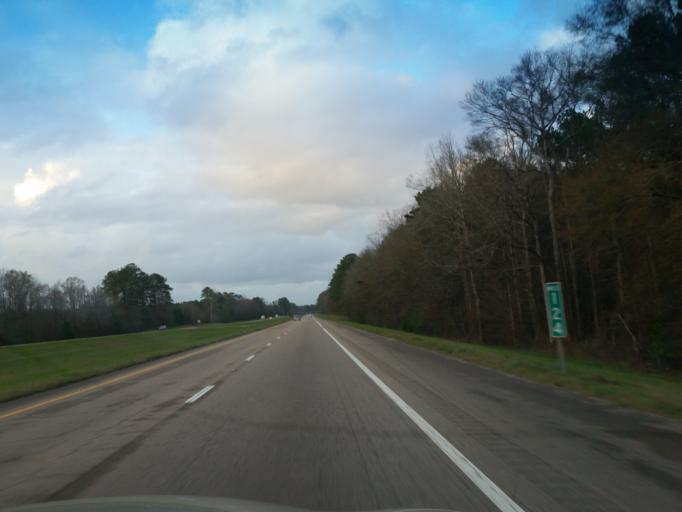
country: US
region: Mississippi
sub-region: Clarke County
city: Stonewall
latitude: 32.0269
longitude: -88.9222
